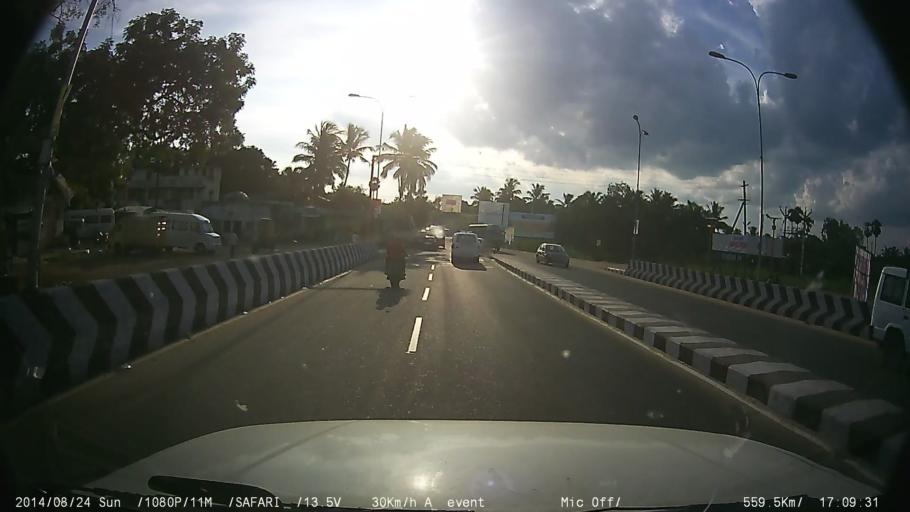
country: IN
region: Tamil Nadu
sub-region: Kancheepuram
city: Vandalur
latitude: 12.8933
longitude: 80.0826
